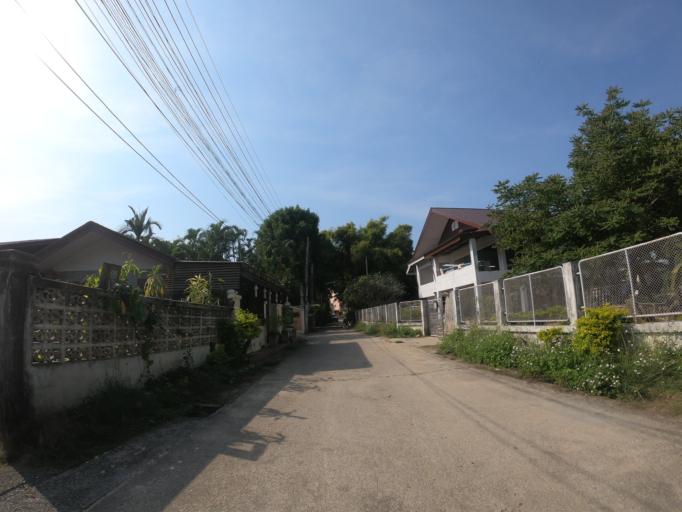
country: TH
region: Chiang Mai
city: Chiang Mai
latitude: 18.7730
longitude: 99.0141
